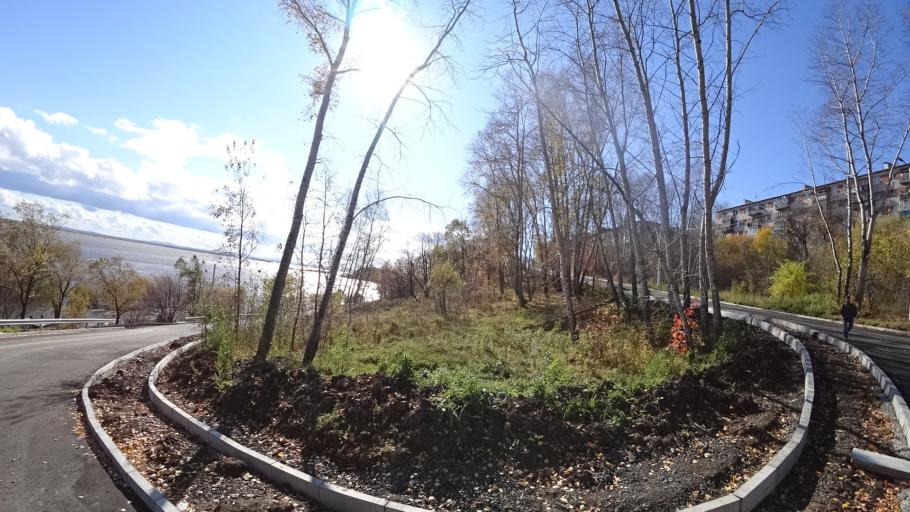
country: RU
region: Khabarovsk Krai
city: Amursk
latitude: 50.2165
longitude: 136.9072
